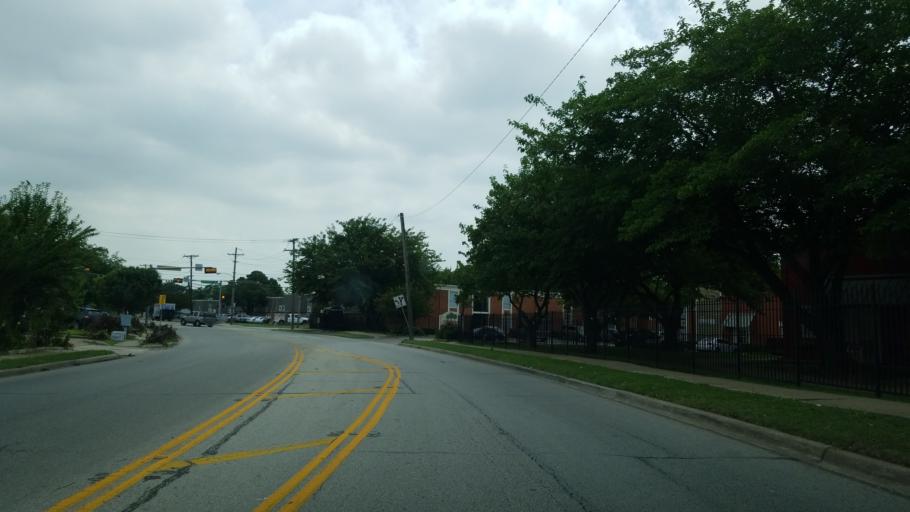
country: US
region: Texas
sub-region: Dallas County
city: Farmers Branch
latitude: 32.9047
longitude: -96.8811
